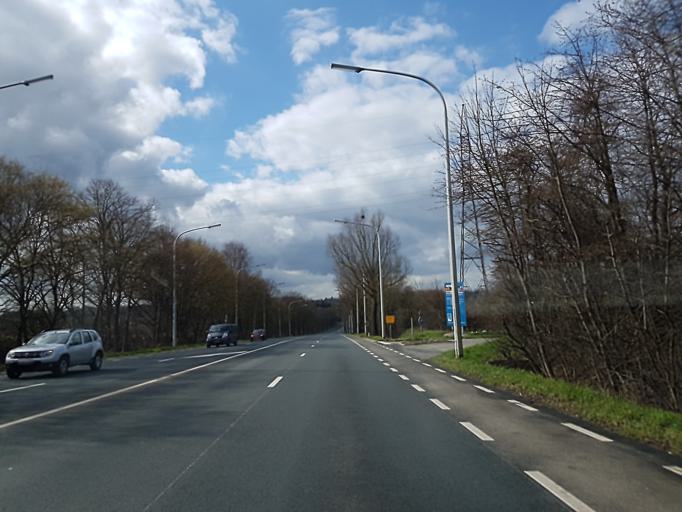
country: BE
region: Wallonia
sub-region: Province de Namur
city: Namur
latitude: 50.4747
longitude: 4.8083
